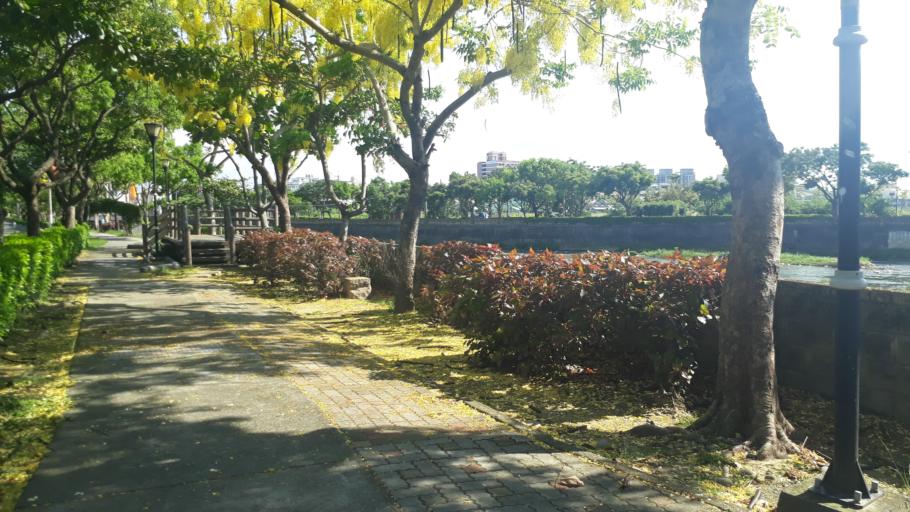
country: TW
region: Taiwan
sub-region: Taichung City
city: Taichung
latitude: 24.1085
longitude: 120.6313
